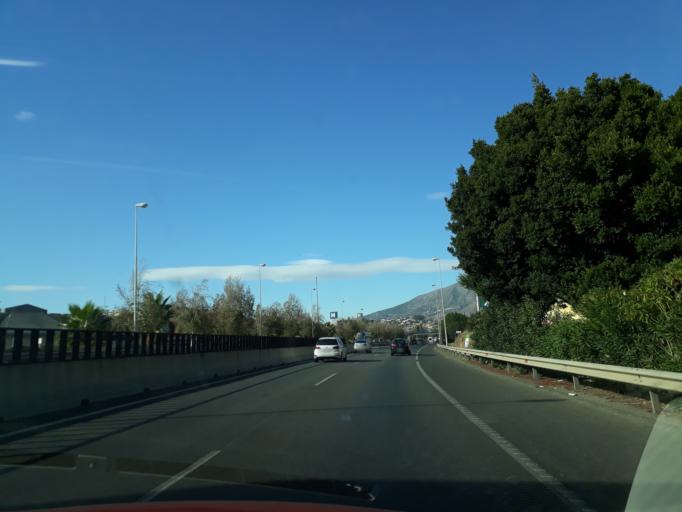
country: ES
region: Andalusia
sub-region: Provincia de Malaga
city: Fuengirola
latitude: 36.5334
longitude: -4.6320
